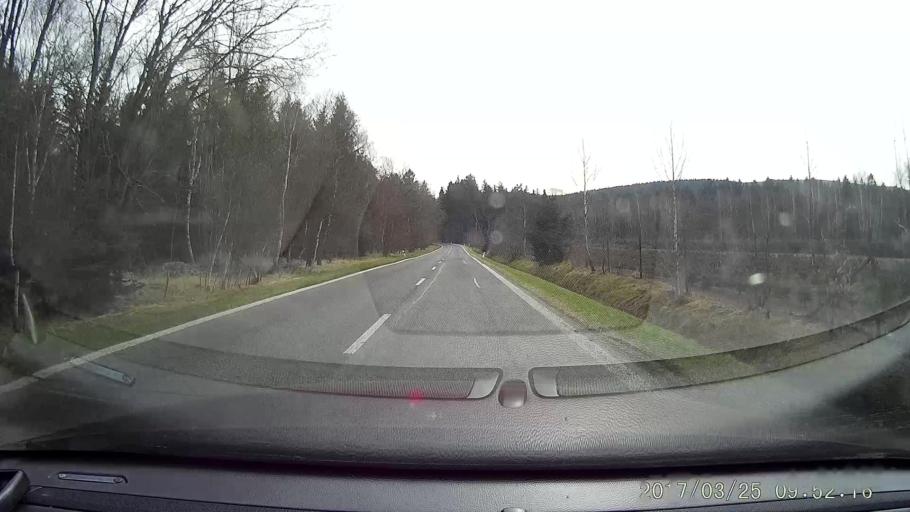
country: CZ
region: Liberecky
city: Nove Mesto pod Smrkem
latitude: 50.9219
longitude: 15.2568
